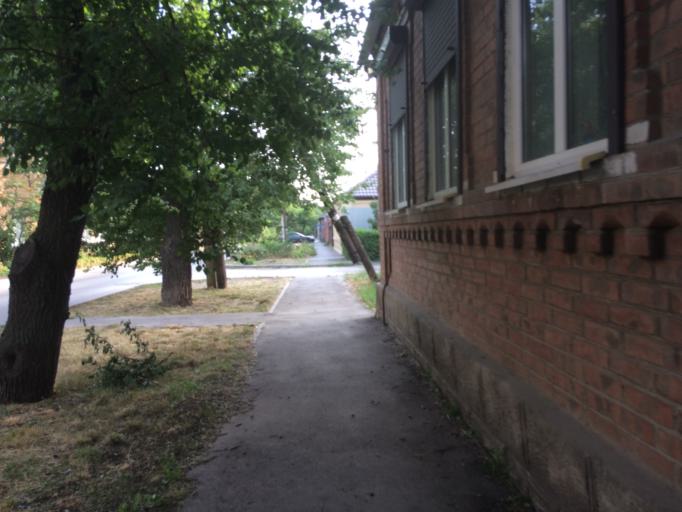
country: RU
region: Rostov
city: Rostov-na-Donu
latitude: 47.2086
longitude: 39.6545
